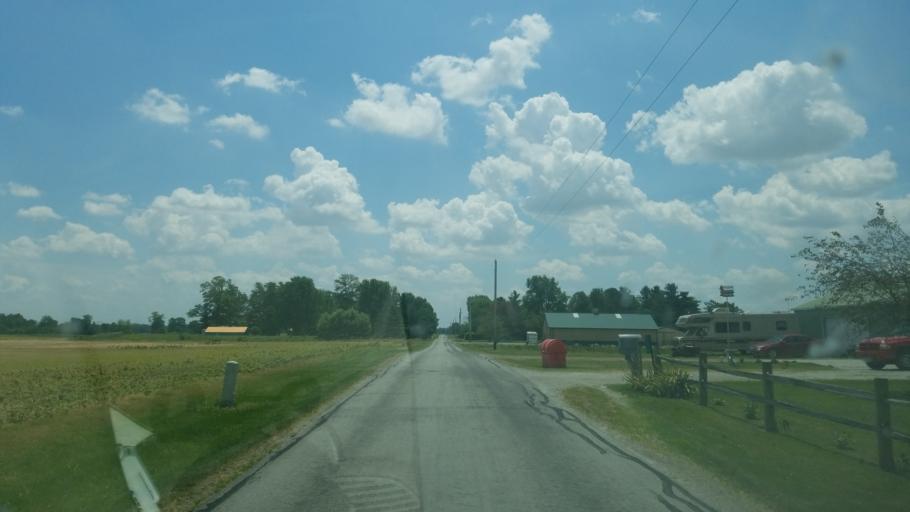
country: US
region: Ohio
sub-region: Hardin County
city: Kenton
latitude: 40.6222
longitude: -83.5601
